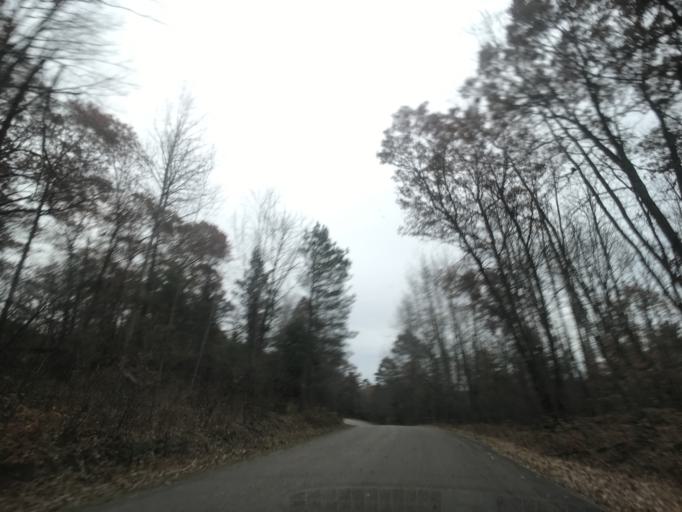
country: US
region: Michigan
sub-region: Dickinson County
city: Kingsford
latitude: 45.3772
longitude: -88.3216
